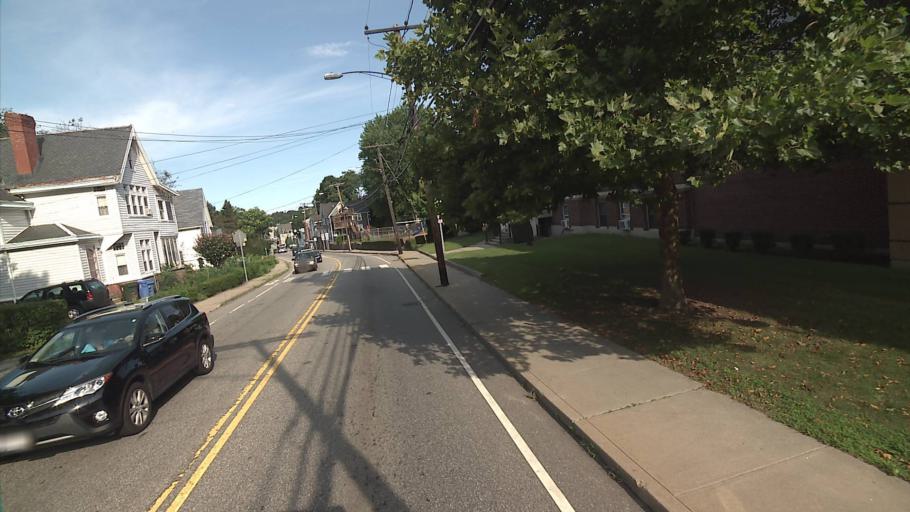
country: US
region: Connecticut
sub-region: New London County
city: Norwich
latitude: 41.5225
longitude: -72.0625
